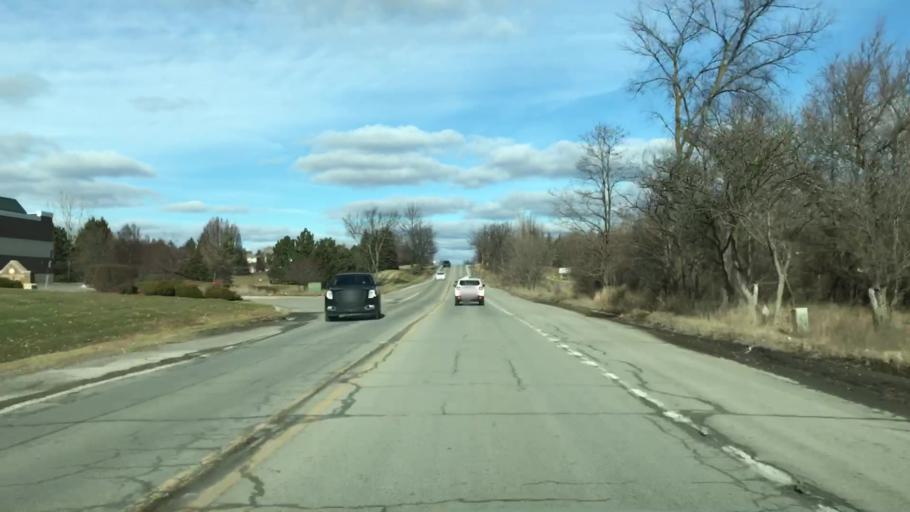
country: US
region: Michigan
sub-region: Oakland County
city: Auburn Hills
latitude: 42.7262
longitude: -83.1963
